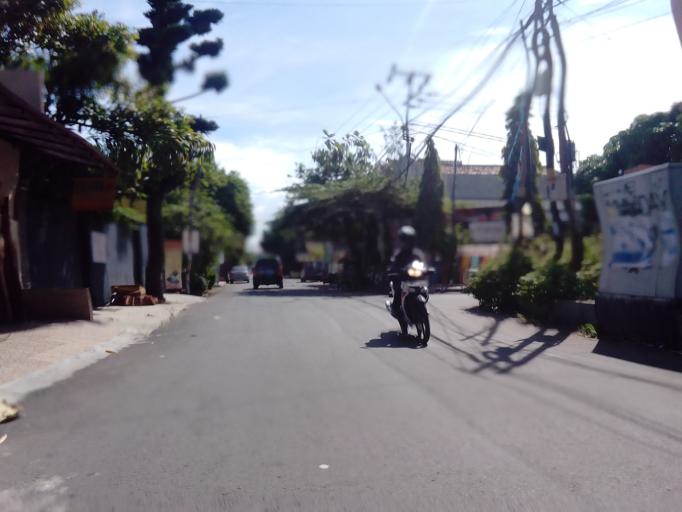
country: ID
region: West Java
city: Bandung
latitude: -6.9477
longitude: 107.6652
